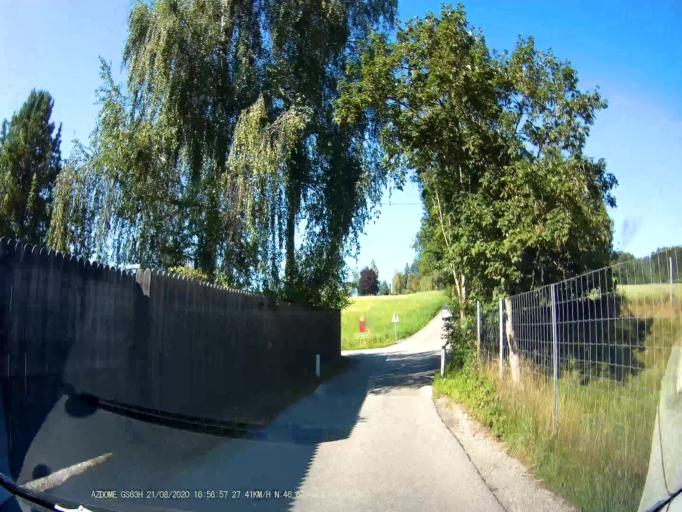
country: AT
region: Carinthia
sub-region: Politischer Bezirk Klagenfurt Land
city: Moosburg
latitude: 46.6728
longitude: 14.1560
